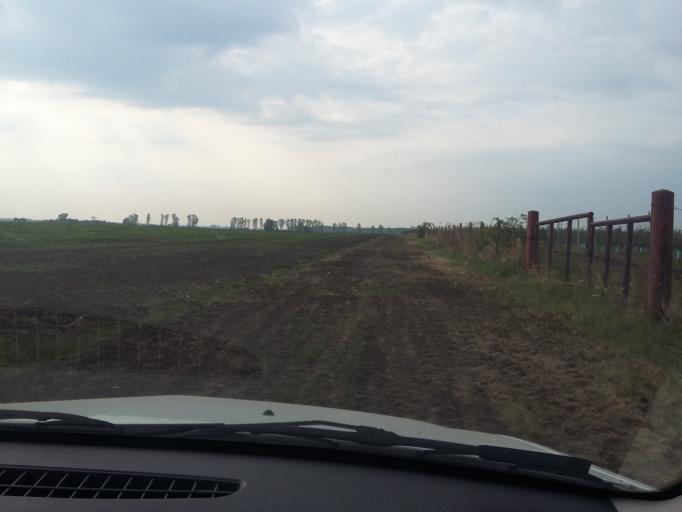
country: HU
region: Borsod-Abauj-Zemplen
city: Taktaharkany
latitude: 48.1282
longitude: 21.1071
